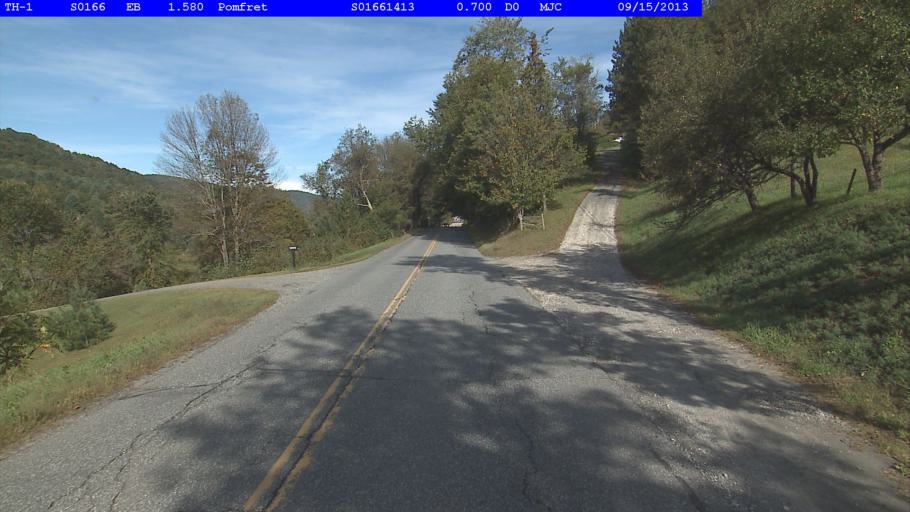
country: US
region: Vermont
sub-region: Windsor County
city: Woodstock
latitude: 43.6597
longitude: -72.5332
